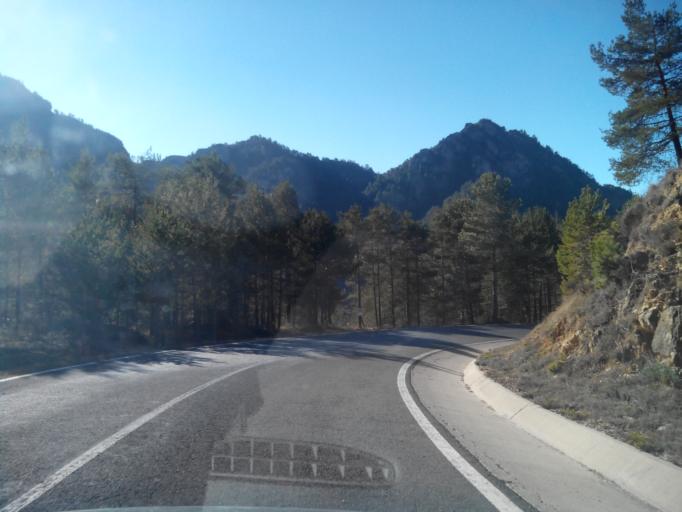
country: ES
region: Catalonia
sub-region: Provincia de Lleida
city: Gosol
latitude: 42.1276
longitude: 1.6289
